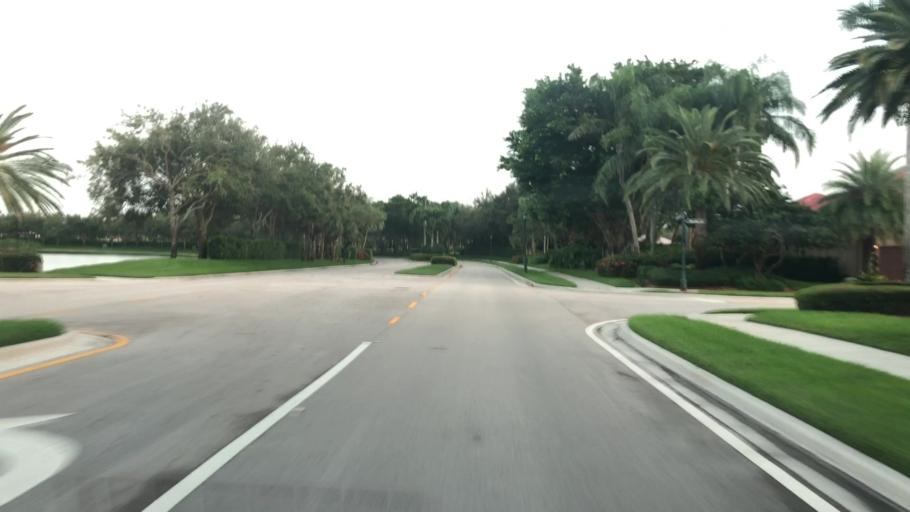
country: US
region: Florida
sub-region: Broward County
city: Weston
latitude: 26.0917
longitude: -80.4006
